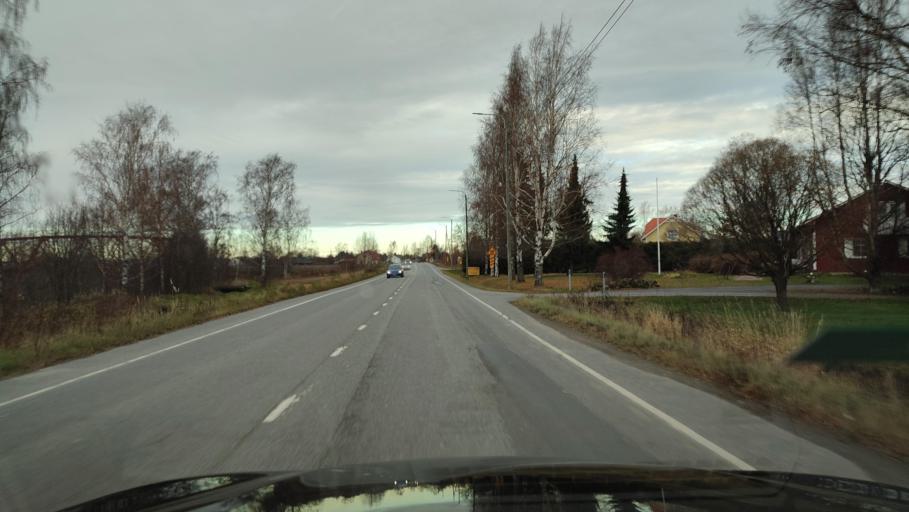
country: FI
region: Ostrobothnia
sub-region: Sydosterbotten
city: Naerpes
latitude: 62.4625
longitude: 21.3563
